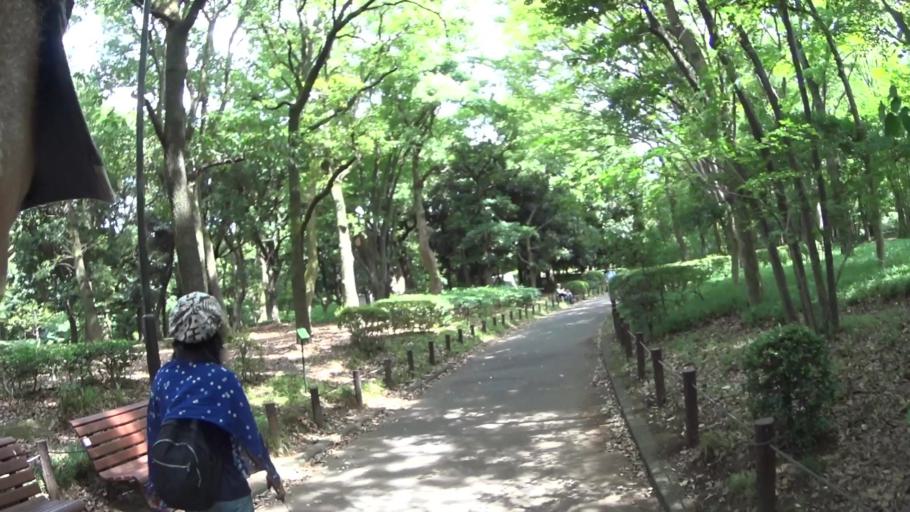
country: JP
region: Tokyo
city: Tokyo
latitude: 35.6922
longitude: 139.7503
